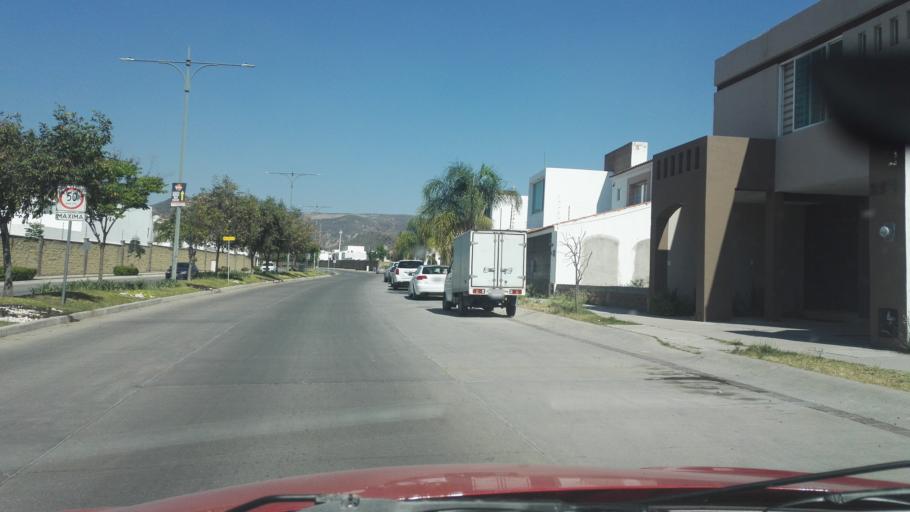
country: MX
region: Guanajuato
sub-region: Leon
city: Medina
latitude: 21.1274
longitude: -101.6093
